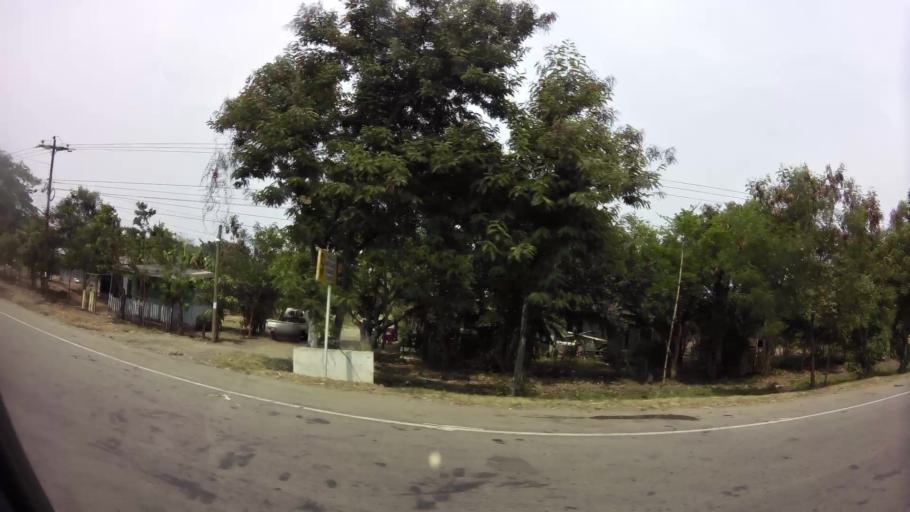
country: HN
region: Cortes
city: Nuevo Chamelecon
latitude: 15.3839
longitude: -87.9902
